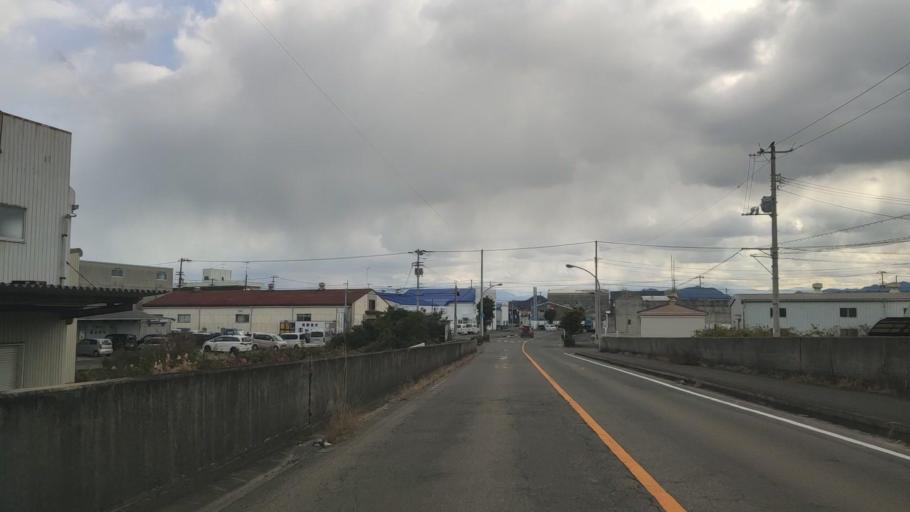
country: JP
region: Ehime
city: Saijo
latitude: 34.0579
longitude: 133.0178
